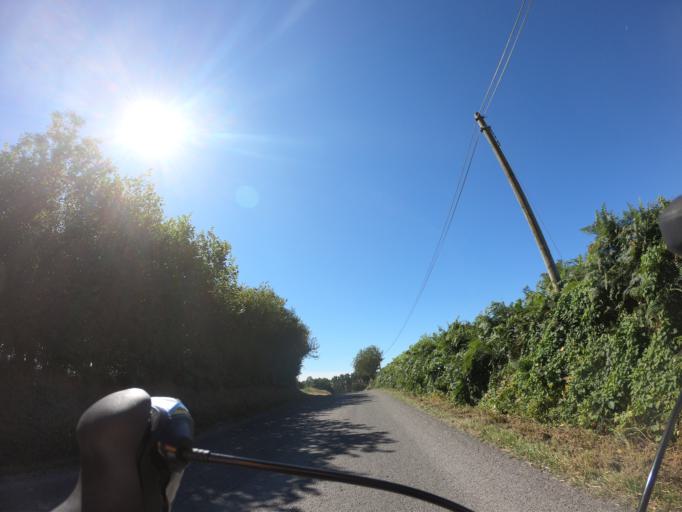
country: FR
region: Lower Normandy
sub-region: Departement de l'Orne
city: Saint-Denis-sur-Sarthon
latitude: 48.5291
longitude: -0.0933
